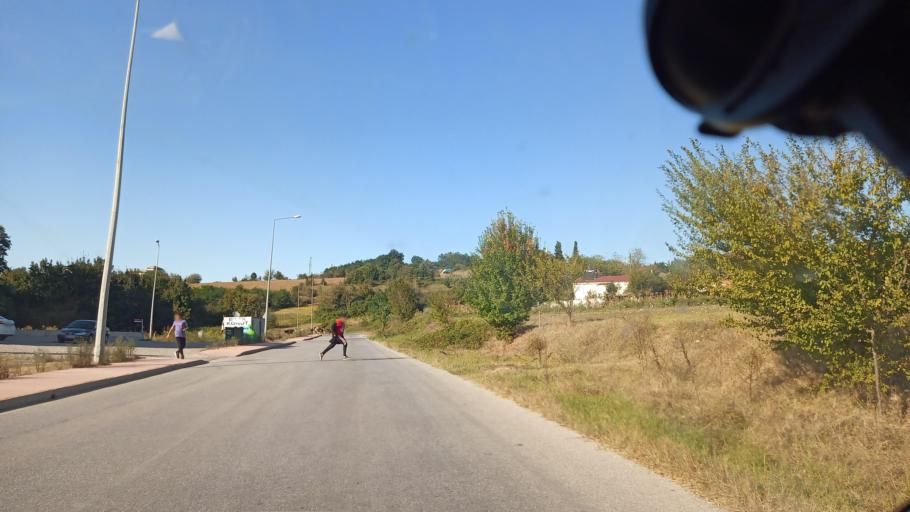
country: TR
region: Sakarya
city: Kazimpasa
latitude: 40.8516
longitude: 30.2792
